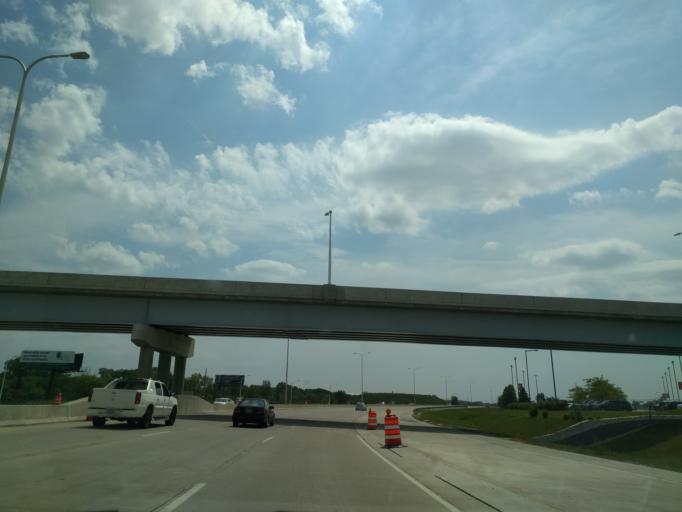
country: US
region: Illinois
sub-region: Cook County
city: Rosemont
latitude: 41.9895
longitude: -87.8799
